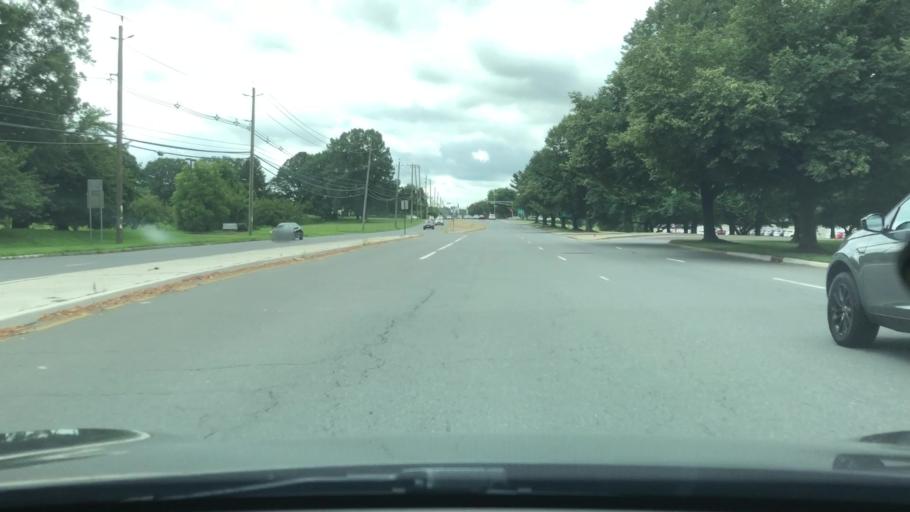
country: US
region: New Jersey
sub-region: Mercer County
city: Lawrenceville
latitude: 40.2926
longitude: -74.6780
